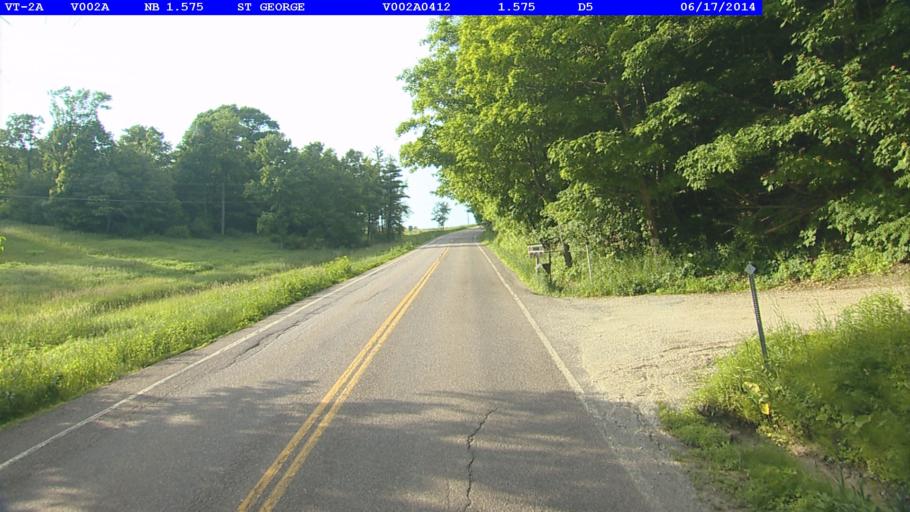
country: US
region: Vermont
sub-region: Chittenden County
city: Hinesburg
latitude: 44.3922
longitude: -73.1278
